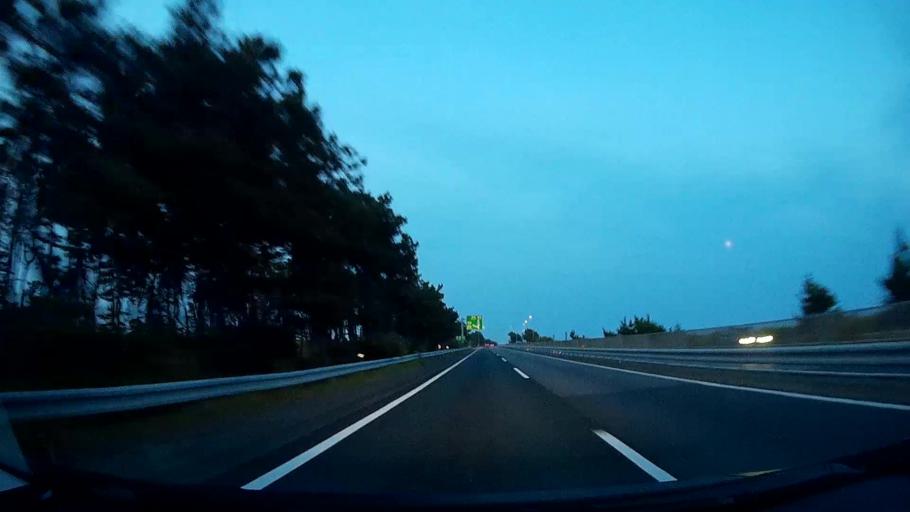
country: JP
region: Shizuoka
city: Kosai-shi
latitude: 34.6775
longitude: 137.6248
